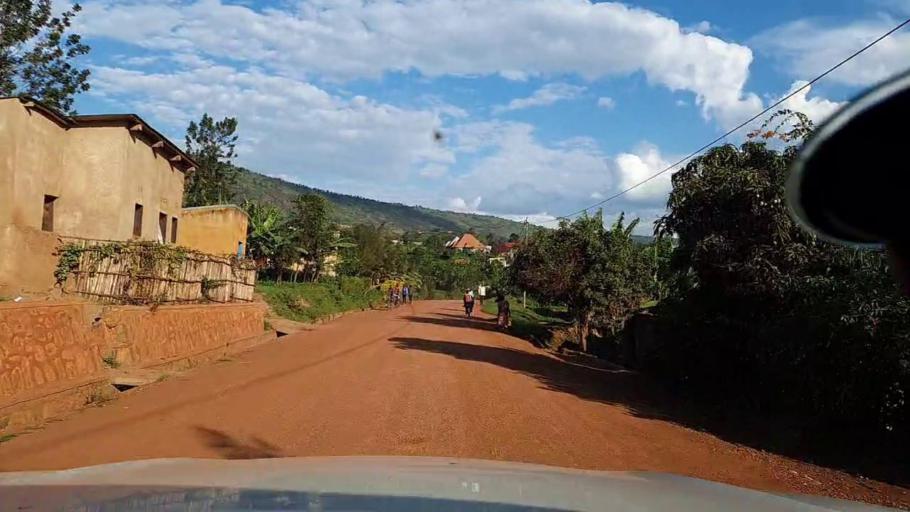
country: RW
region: Kigali
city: Kigali
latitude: -1.8941
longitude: 29.9624
